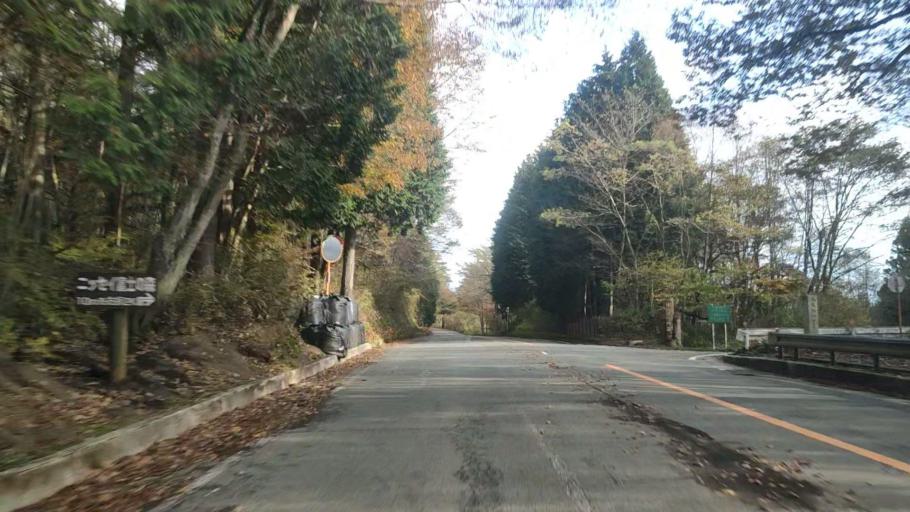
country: JP
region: Shizuoka
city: Fujinomiya
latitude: 35.3013
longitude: 138.6850
